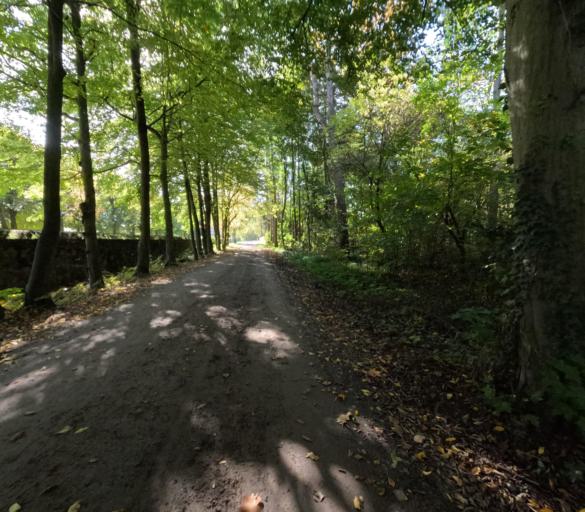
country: DE
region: Saxony
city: Moritzburg
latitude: 51.1711
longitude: 13.6780
